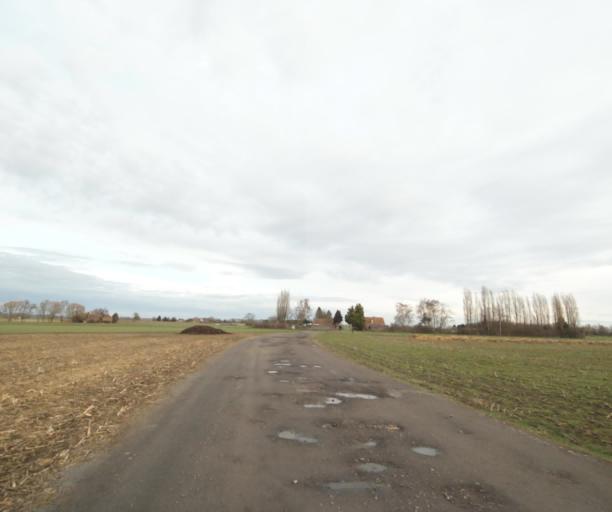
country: FR
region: Nord-Pas-de-Calais
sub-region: Departement du Nord
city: Hergnies
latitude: 50.4826
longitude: 3.5484
